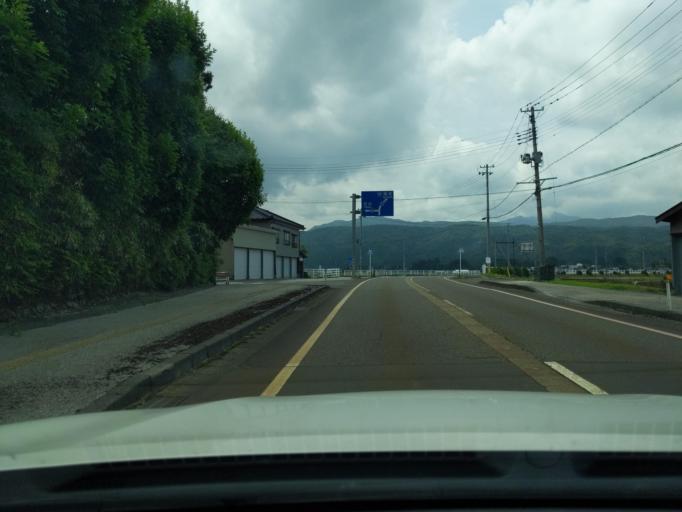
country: JP
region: Niigata
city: Kashiwazaki
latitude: 37.3306
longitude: 138.5757
